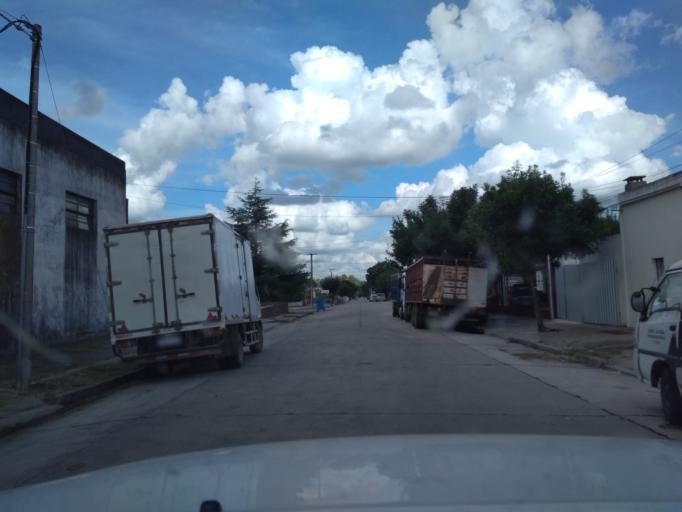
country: UY
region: Florida
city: Florida
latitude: -34.0913
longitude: -56.2157
